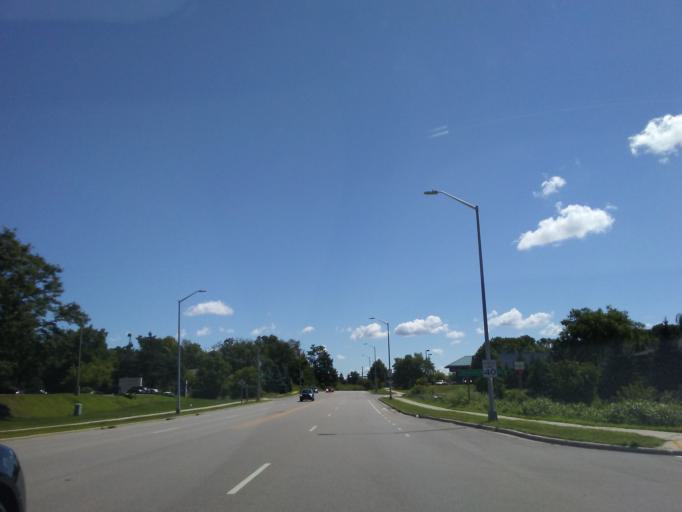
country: US
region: Wisconsin
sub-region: Dane County
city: Madison
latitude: 43.0157
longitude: -89.4286
